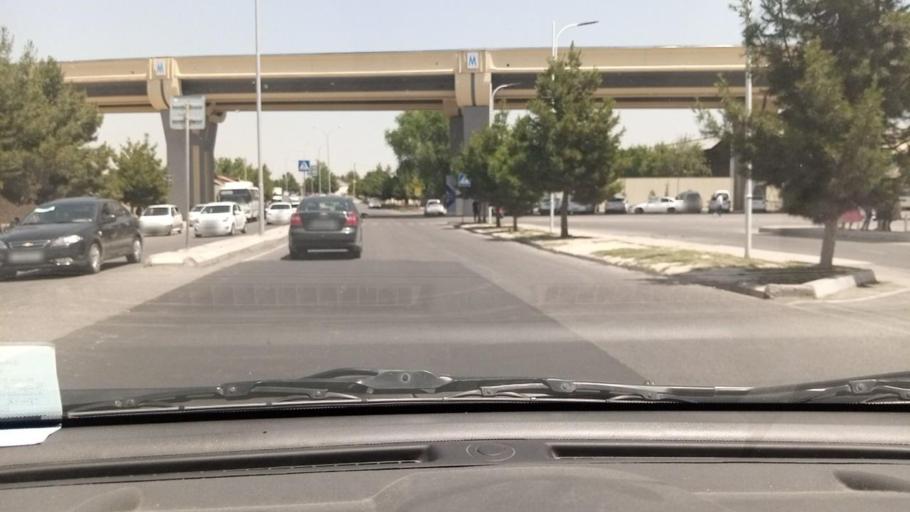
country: UZ
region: Toshkent Shahri
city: Tashkent
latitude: 41.2393
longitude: 69.1944
